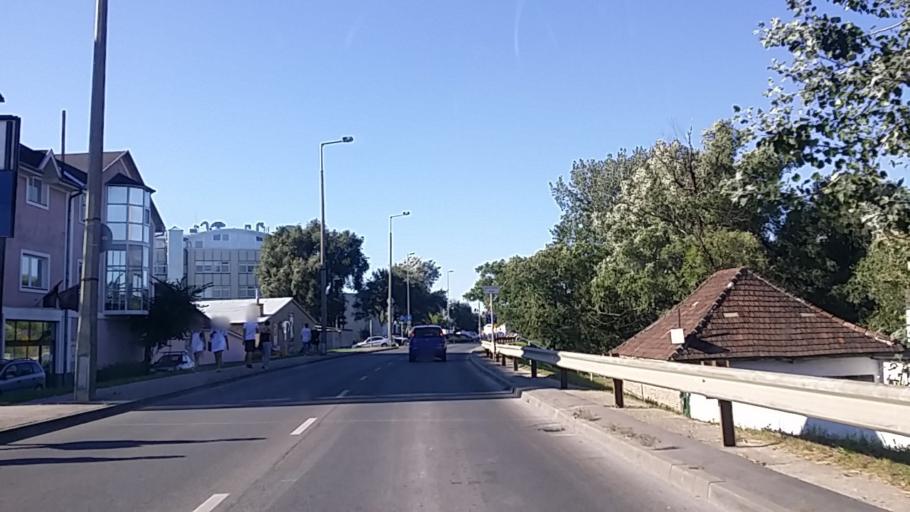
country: HU
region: Budapest
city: Budapest III. keruelet
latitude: 47.5507
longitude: 19.0477
